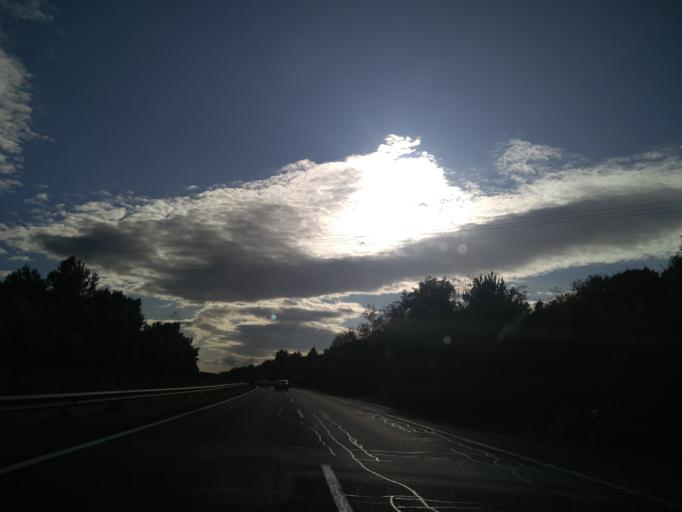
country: HU
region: Fejer
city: Baracska
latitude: 47.3166
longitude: 18.7536
